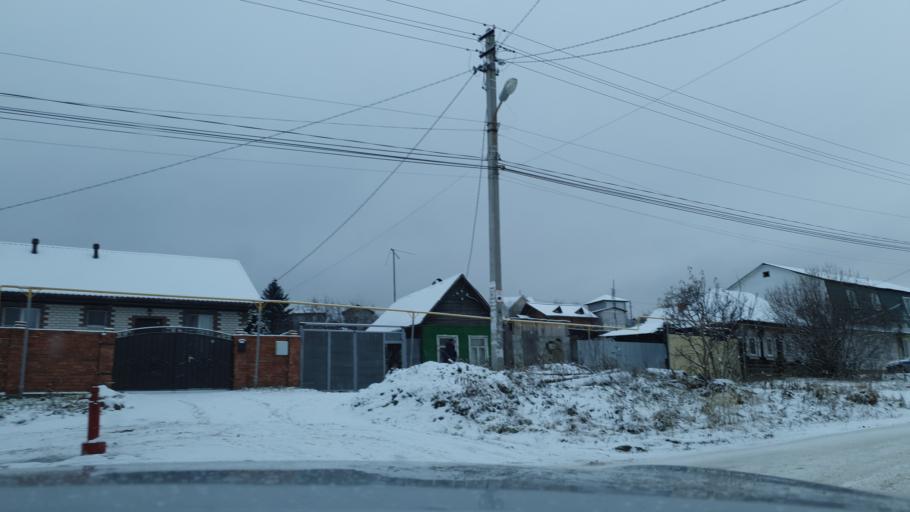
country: RU
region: Sverdlovsk
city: Istok
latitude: 56.7475
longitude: 60.6997
